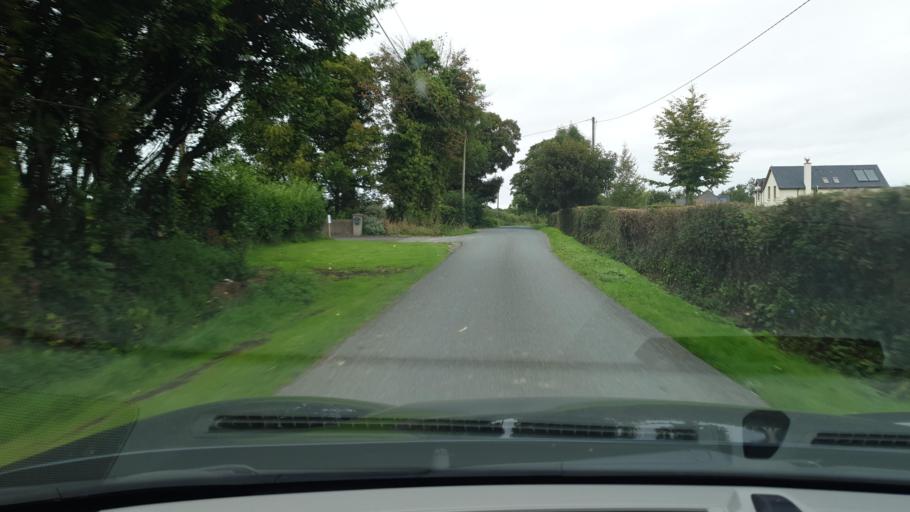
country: IE
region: Leinster
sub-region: An Mhi
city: Ratoath
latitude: 53.5069
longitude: -6.4875
